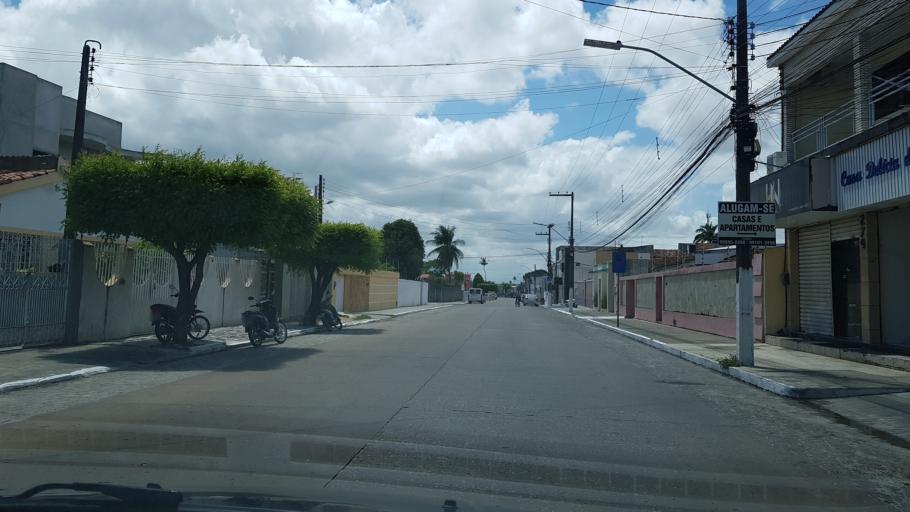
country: BR
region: Alagoas
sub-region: Penedo
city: Penedo
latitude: -10.2819
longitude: -36.5644
